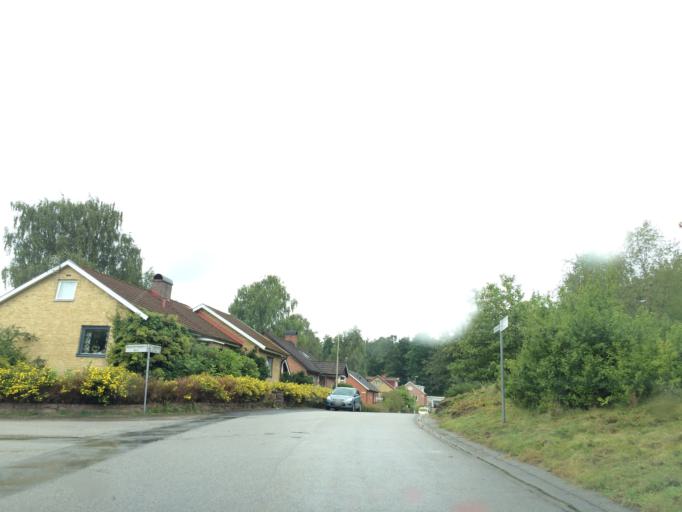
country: SE
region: Vaestra Goetaland
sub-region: Trollhattan
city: Trollhattan
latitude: 58.2817
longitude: 12.2573
